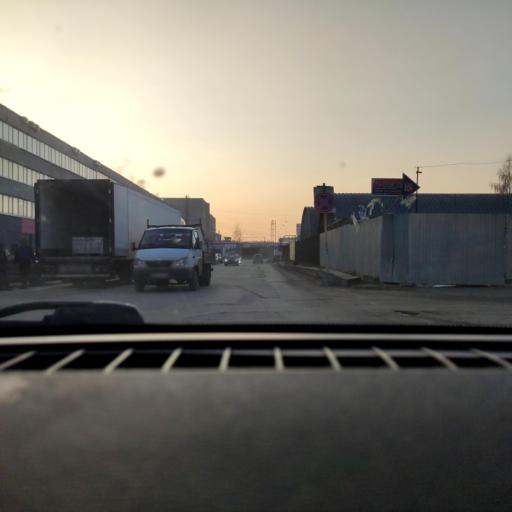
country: RU
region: Perm
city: Froly
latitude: 57.9598
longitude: 56.2749
